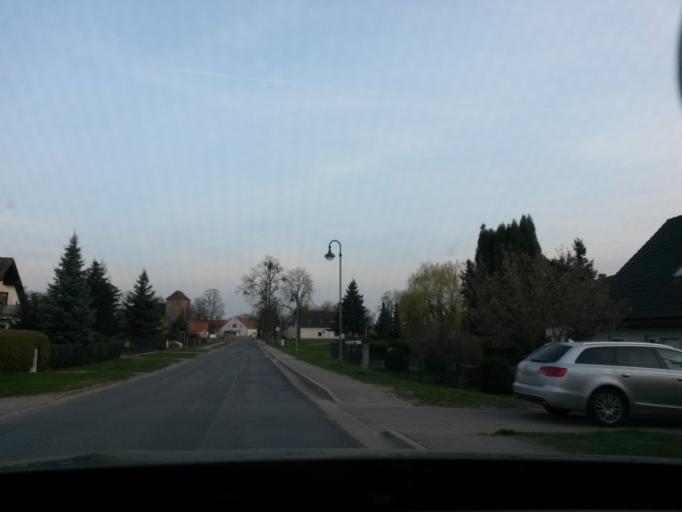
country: DE
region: Brandenburg
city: Protzel
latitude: 52.5924
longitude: 13.9488
